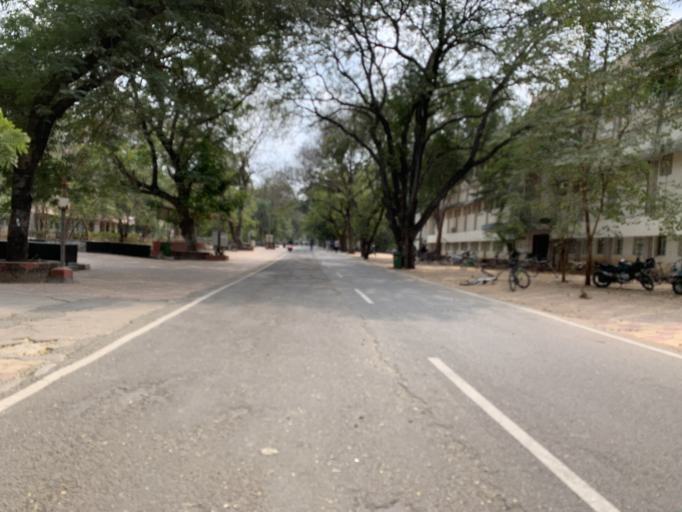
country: IN
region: Telangana
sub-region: Warangal
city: Warangal
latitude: 17.9836
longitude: 79.5321
